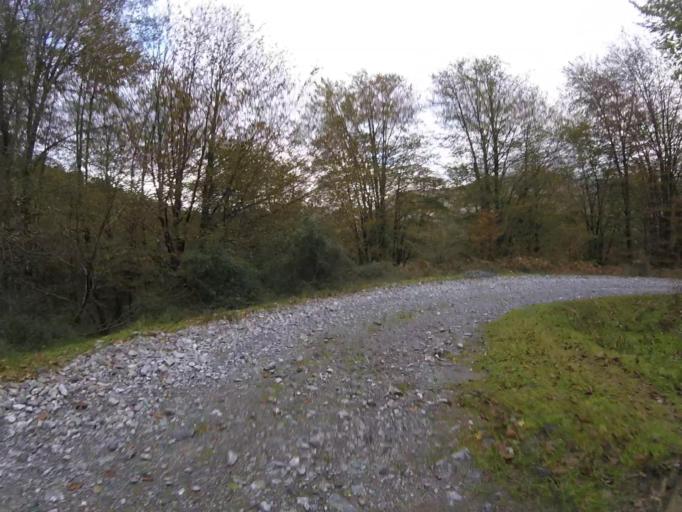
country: ES
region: Navarre
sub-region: Provincia de Navarra
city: Goizueta
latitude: 43.1811
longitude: -1.8087
